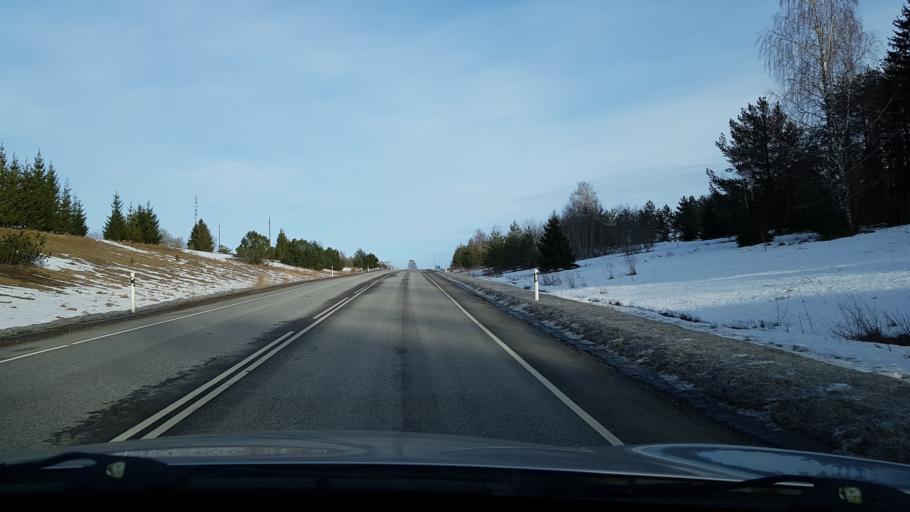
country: EE
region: Viljandimaa
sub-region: Viljandi linn
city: Viljandi
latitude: 58.3424
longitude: 25.4896
